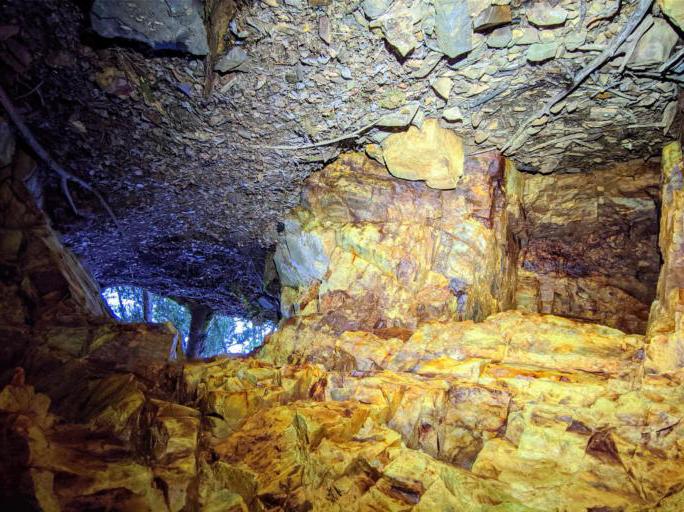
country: NO
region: Akershus
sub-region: Eidsvoll
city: Eidsvoll
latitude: 60.3871
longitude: 11.2103
